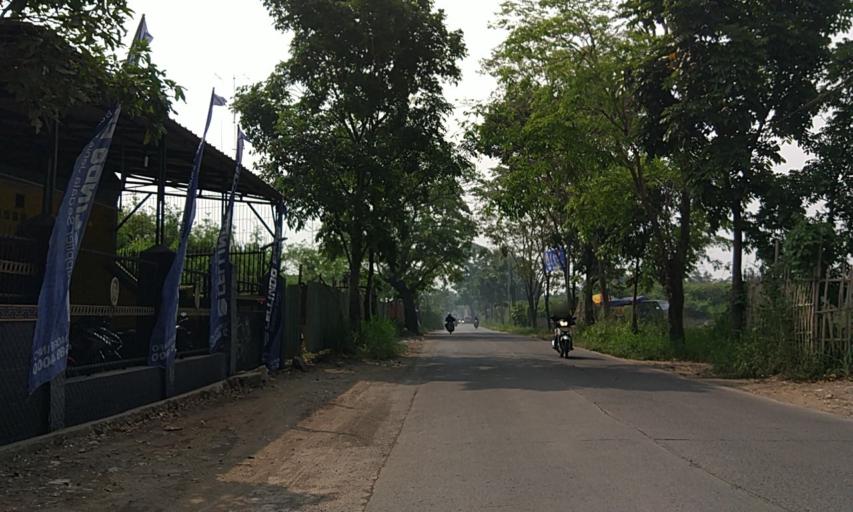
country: ID
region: West Java
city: Soreang
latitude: -7.0362
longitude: 107.5511
